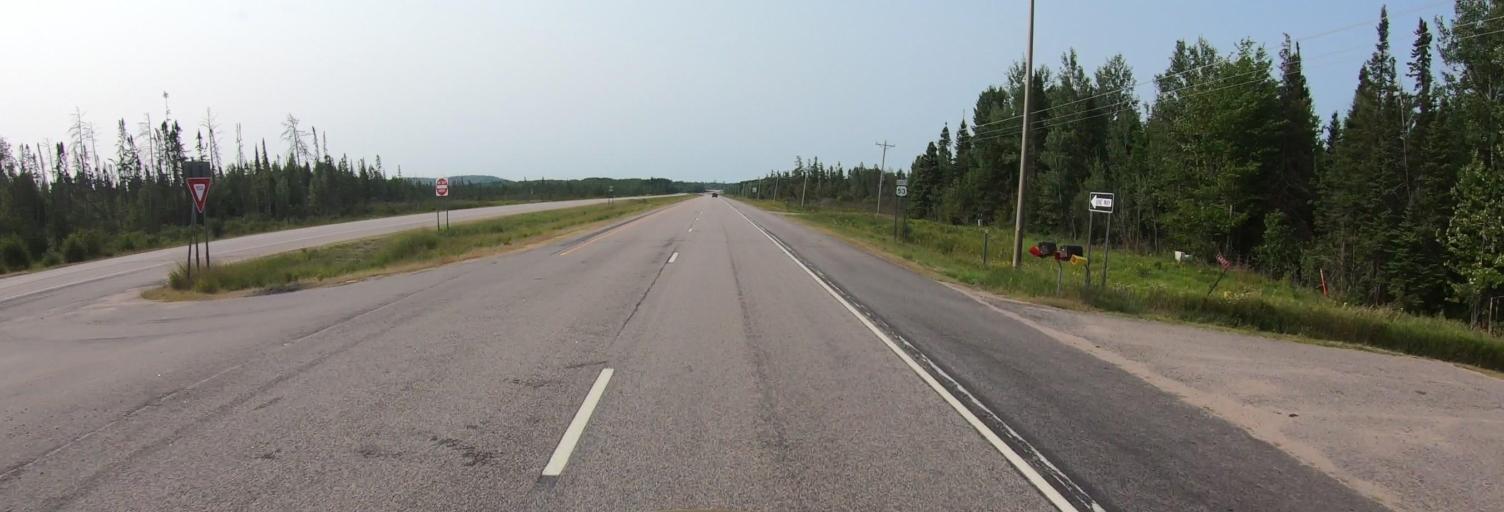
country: US
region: Minnesota
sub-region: Saint Louis County
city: Parkville
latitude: 47.6142
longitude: -92.5543
